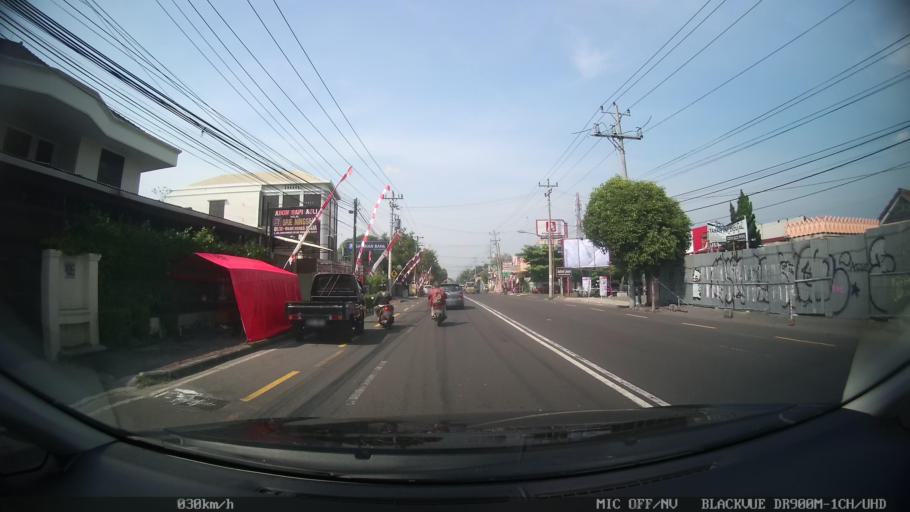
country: ID
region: Daerah Istimewa Yogyakarta
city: Yogyakarta
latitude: -7.7914
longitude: 110.3538
